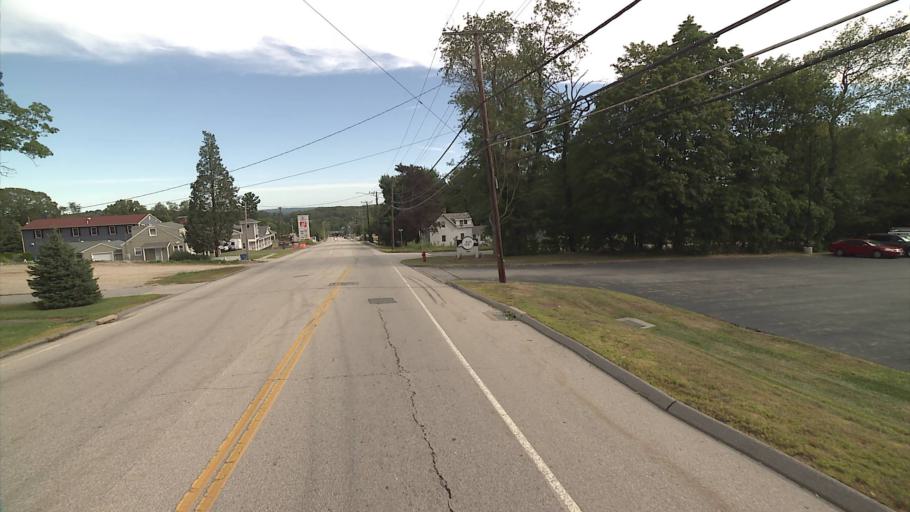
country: US
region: Connecticut
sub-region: New London County
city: Oxoboxo River
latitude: 41.4757
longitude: -72.0999
